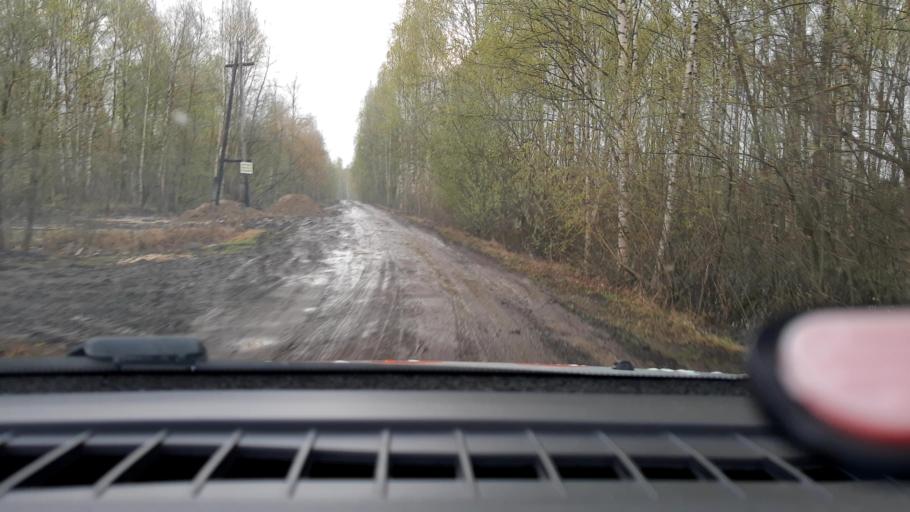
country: RU
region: Nizjnij Novgorod
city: Gorbatovka
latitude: 56.3013
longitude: 43.7698
